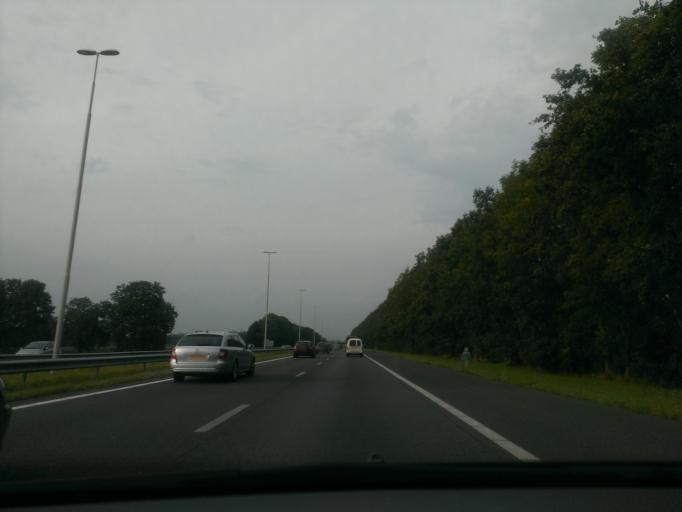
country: NL
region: Gelderland
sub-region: Gemeente Epe
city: Emst
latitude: 52.3012
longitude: 6.0088
